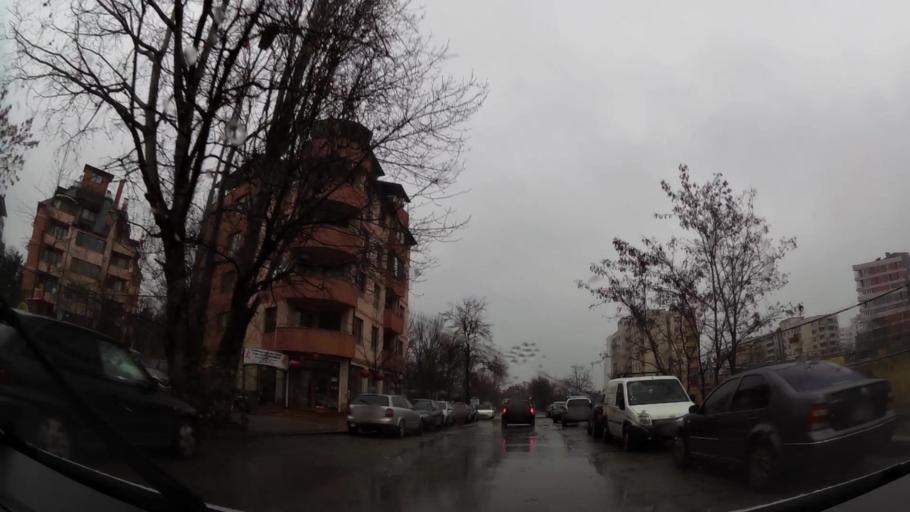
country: BG
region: Sofia-Capital
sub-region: Stolichna Obshtina
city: Sofia
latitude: 42.6446
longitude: 23.3368
